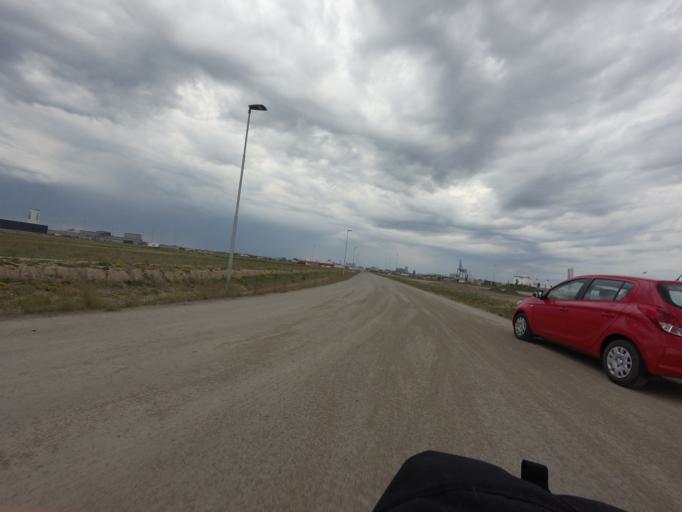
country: SE
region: Skane
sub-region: Malmo
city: Malmoe
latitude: 55.6324
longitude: 12.9944
